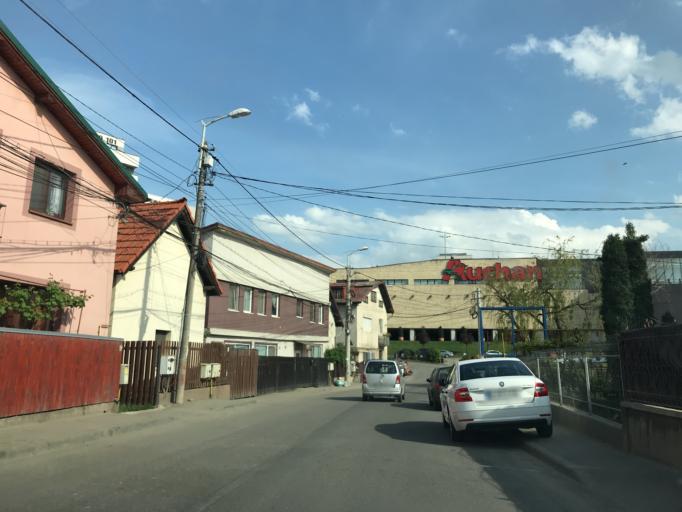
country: RO
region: Cluj
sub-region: Municipiul Cluj-Napoca
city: Cluj-Napoca
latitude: 46.7744
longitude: 23.6272
